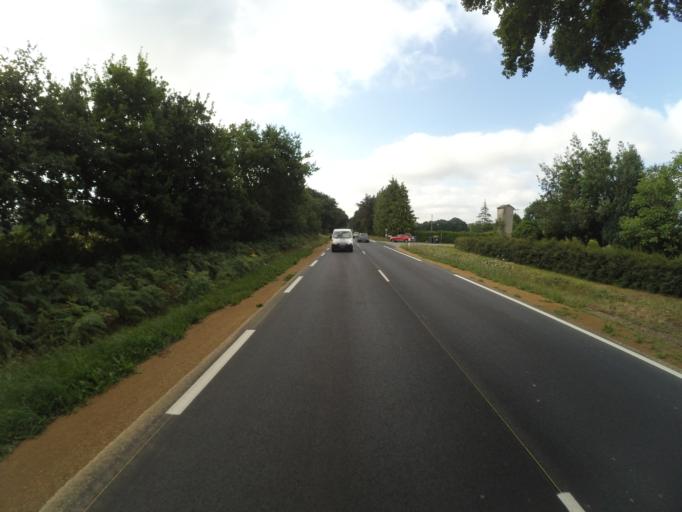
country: FR
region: Brittany
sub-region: Departement du Finistere
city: Redene
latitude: 47.8392
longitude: -3.5047
